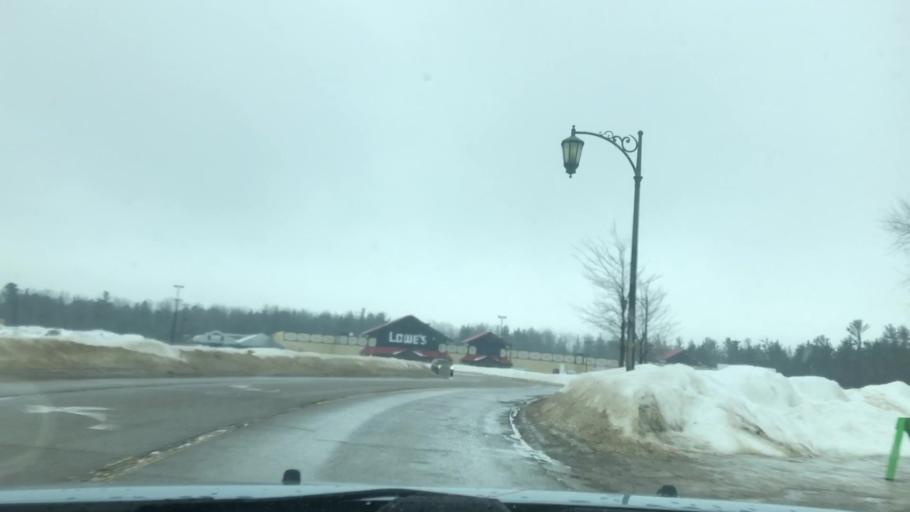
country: US
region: Michigan
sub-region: Otsego County
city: Gaylord
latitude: 45.0252
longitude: -84.6941
